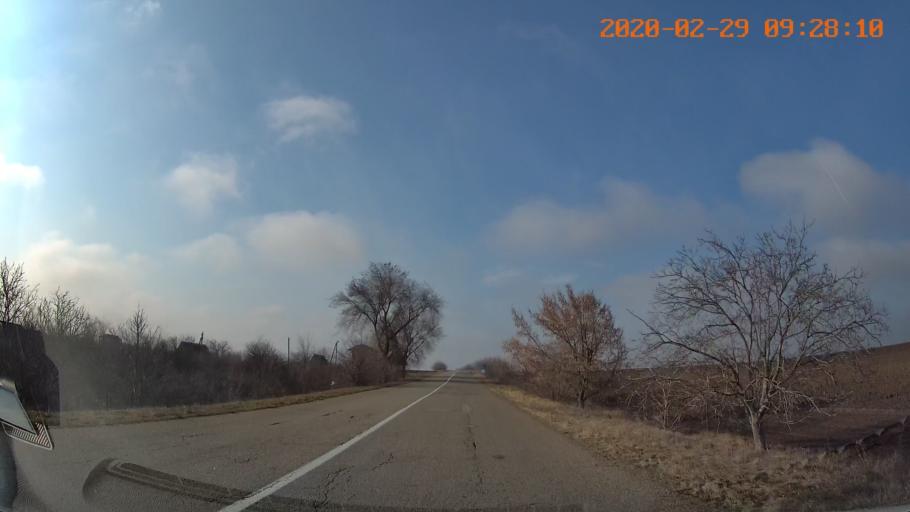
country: MD
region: Telenesti
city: Pervomaisc
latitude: 46.6920
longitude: 29.9323
